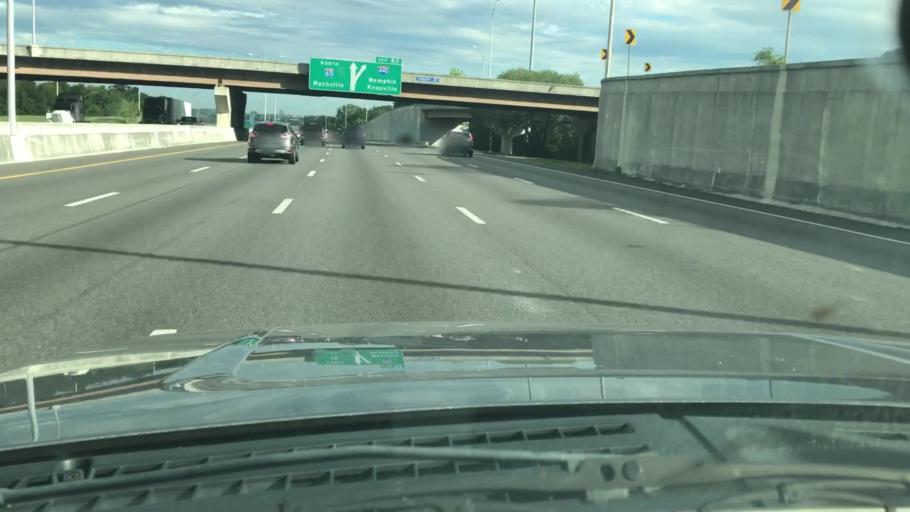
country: US
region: Tennessee
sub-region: Davidson County
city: Oak Hill
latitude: 36.1008
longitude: -86.7643
